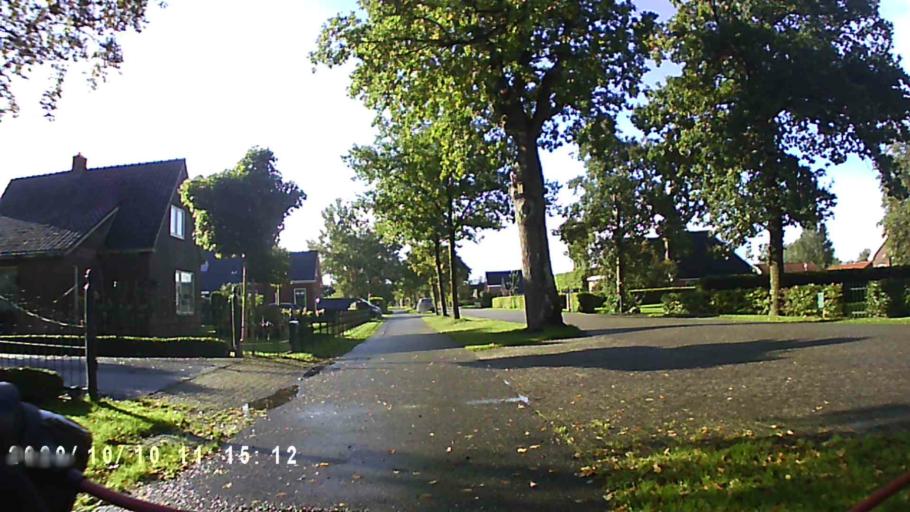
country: NL
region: Friesland
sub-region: Gemeente Smallingerland
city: Drachtstercompagnie
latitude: 53.1034
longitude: 6.2018
